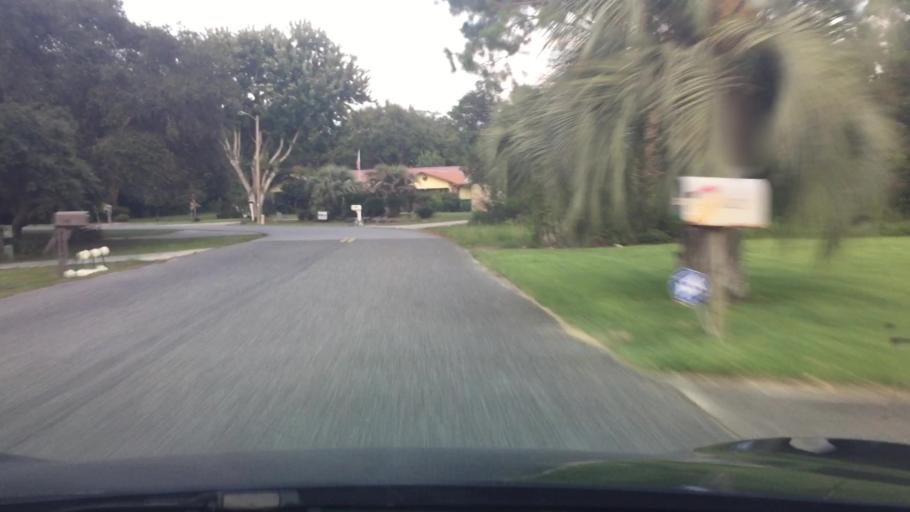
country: US
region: Florida
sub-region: Bay County
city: Laguna Beach
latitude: 30.2523
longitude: -85.9426
